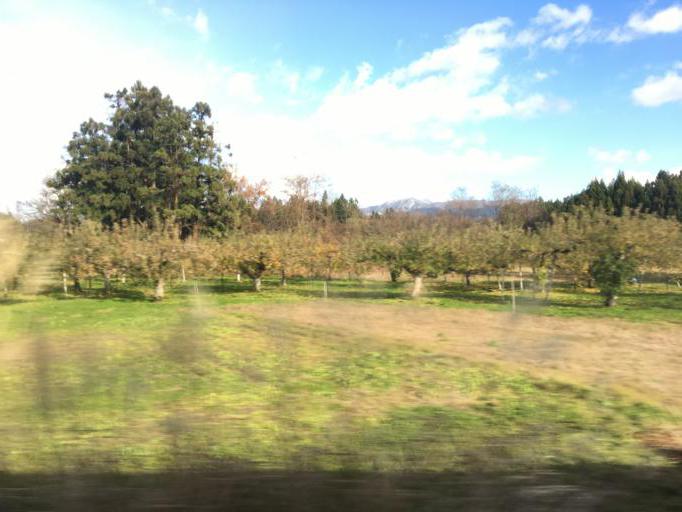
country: JP
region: Akita
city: Yokotemachi
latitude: 39.3588
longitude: 140.5418
